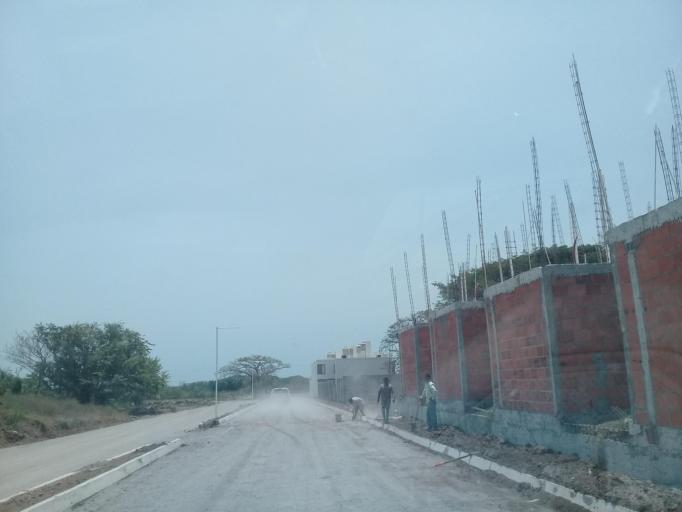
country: MX
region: Veracruz
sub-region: Veracruz
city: Hacienda Sotavento
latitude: 19.1435
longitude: -96.1745
